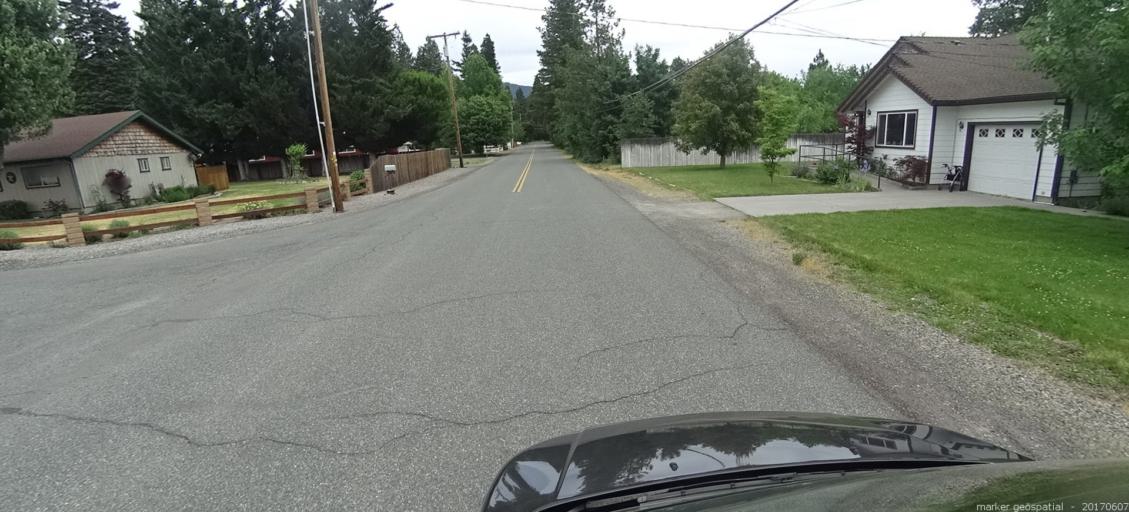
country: US
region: California
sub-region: Siskiyou County
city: Mount Shasta
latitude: 41.3247
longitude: -122.3369
